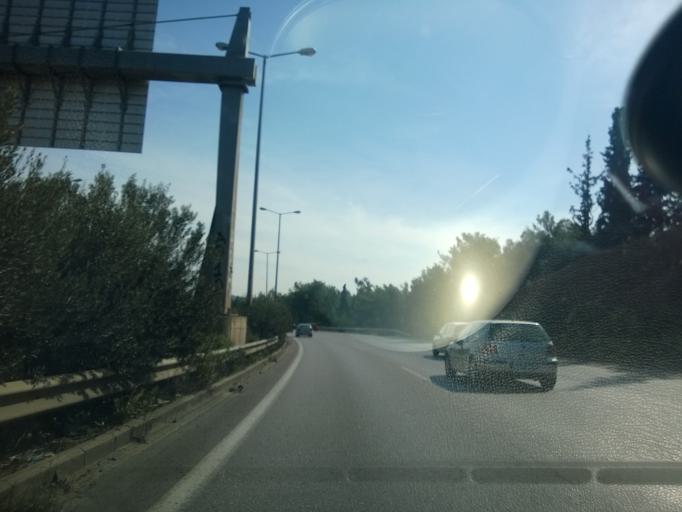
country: GR
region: Central Macedonia
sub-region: Nomos Thessalonikis
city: Triandria
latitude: 40.6170
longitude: 22.9840
